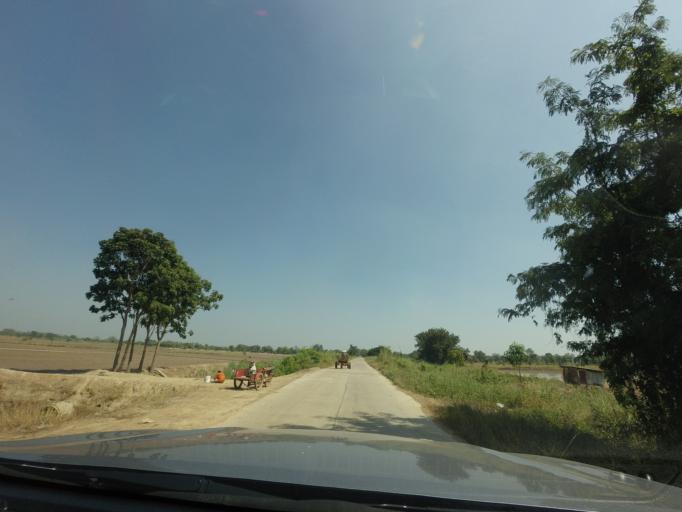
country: TH
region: Sukhothai
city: Sawankhalok
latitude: 17.2751
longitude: 99.8124
